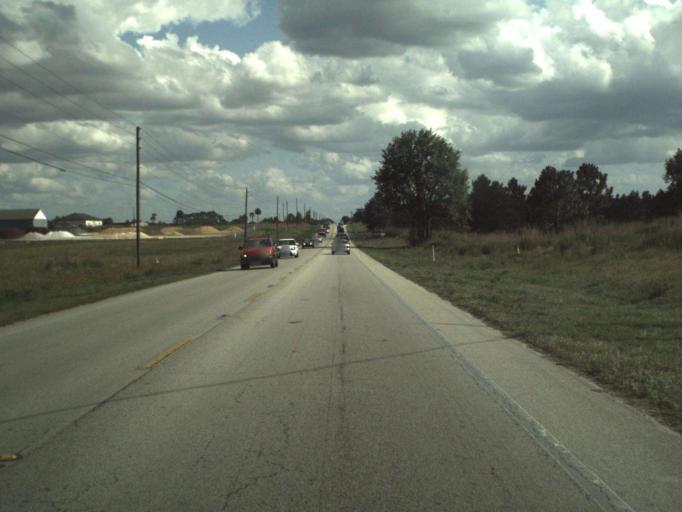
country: US
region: Florida
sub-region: Marion County
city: Silver Springs Shores
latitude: 29.1132
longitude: -82.0536
